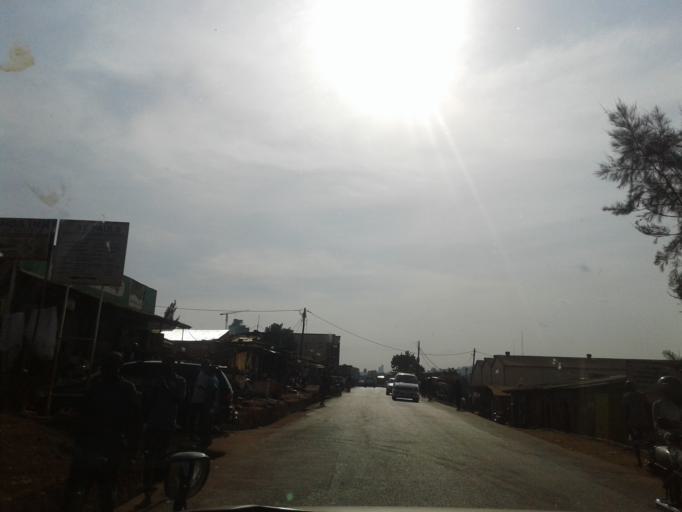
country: UG
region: Central Region
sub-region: Wakiso District
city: Kireka
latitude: 0.3338
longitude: 32.6272
